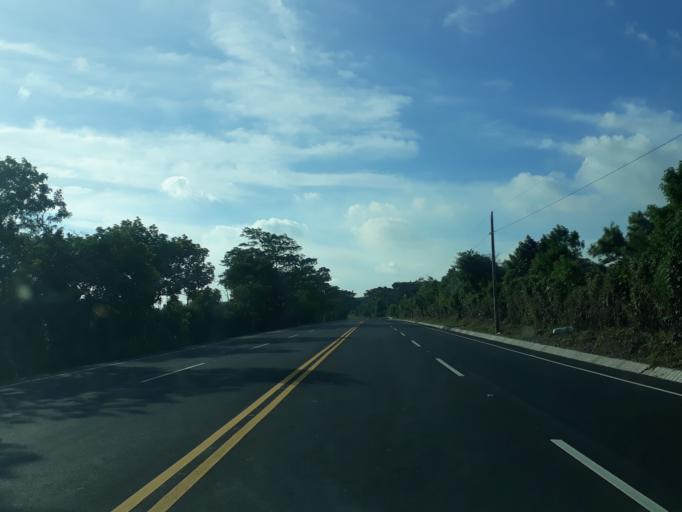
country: NI
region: Carazo
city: Diriamba
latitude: 11.9124
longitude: -86.2681
